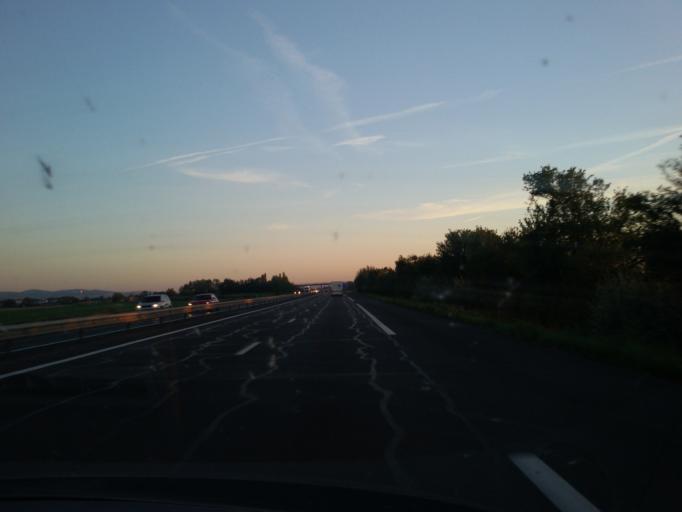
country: FR
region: Auvergne
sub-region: Departement du Puy-de-Dome
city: Gerzat
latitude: 45.8534
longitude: 3.1600
